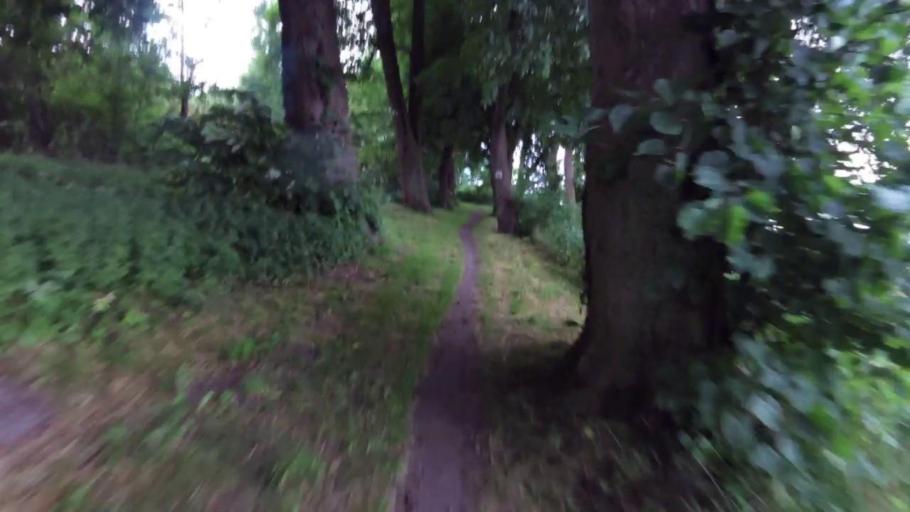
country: PL
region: West Pomeranian Voivodeship
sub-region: Powiat stargardzki
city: Chociwel
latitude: 53.4656
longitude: 15.3384
